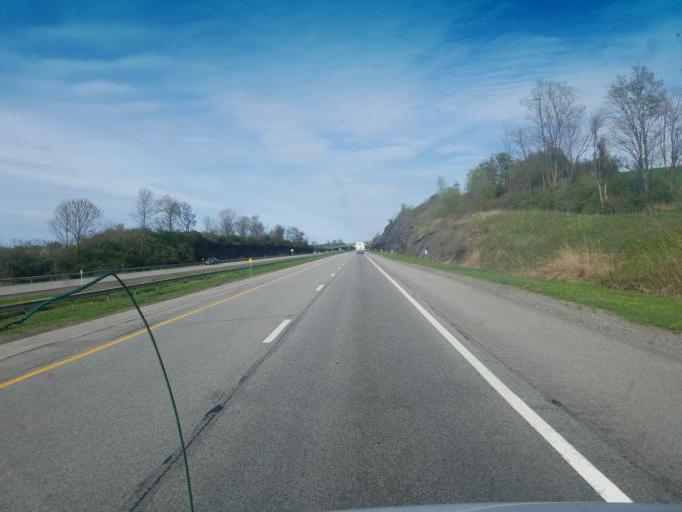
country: US
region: New York
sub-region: Herkimer County
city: Little Falls
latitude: 43.0073
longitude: -74.8727
